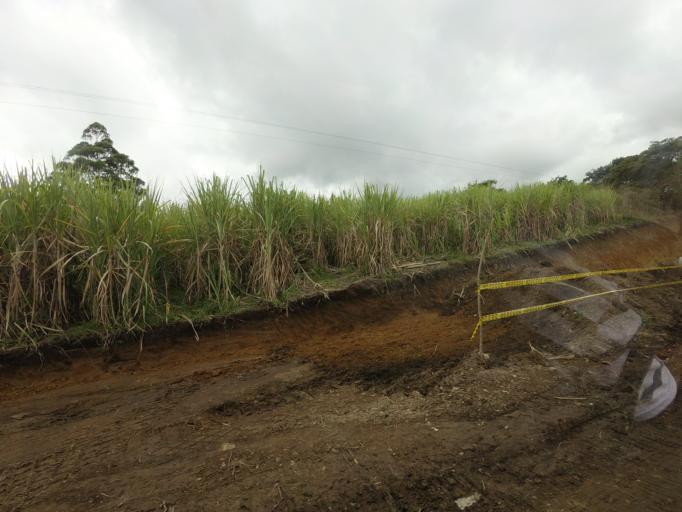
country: CO
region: Huila
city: San Agustin
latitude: 1.9492
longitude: -76.2976
